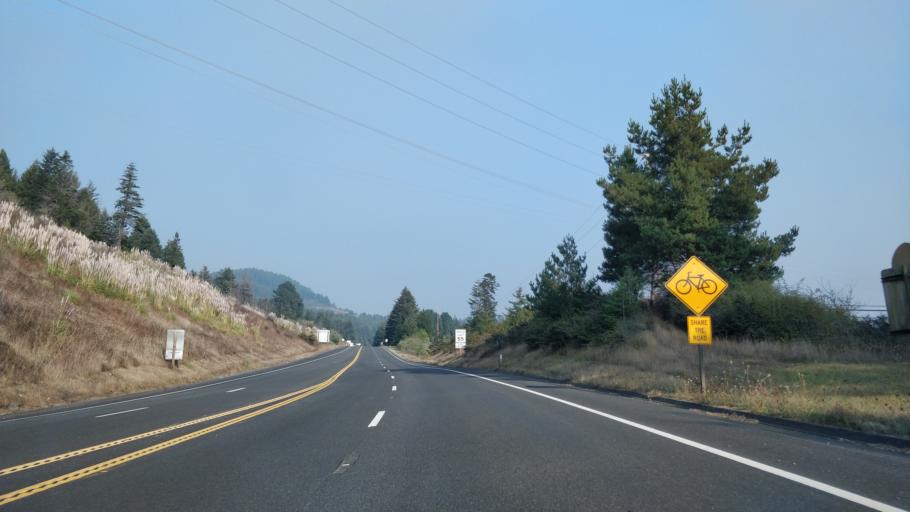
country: US
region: California
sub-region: Humboldt County
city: Blue Lake
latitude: 40.8870
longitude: -123.9916
